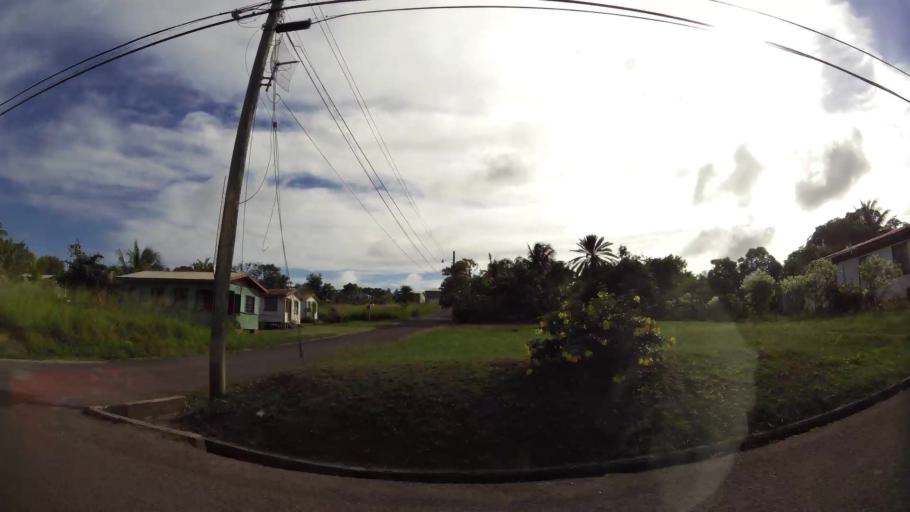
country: AG
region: Saint Peter
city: All Saints
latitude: 17.0505
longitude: -61.7962
